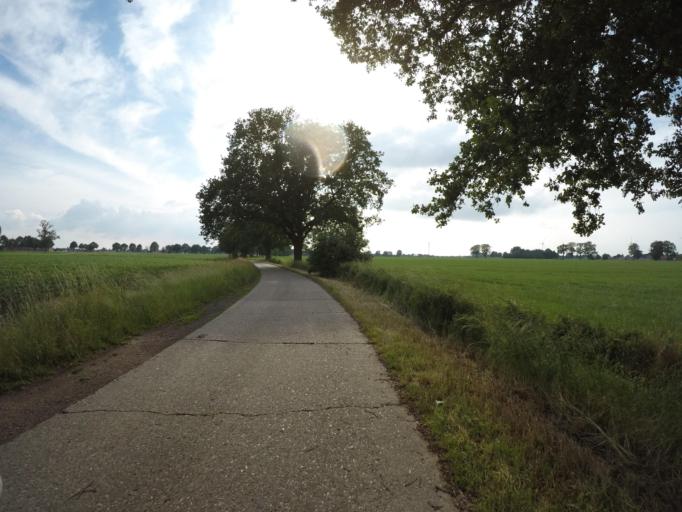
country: BE
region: Flanders
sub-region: Provincie Antwerpen
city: Brecht
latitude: 51.3594
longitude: 4.6829
